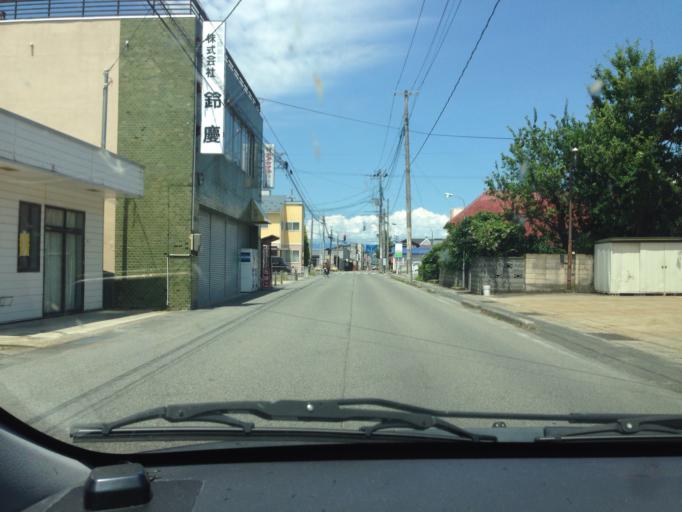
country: JP
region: Fukushima
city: Kitakata
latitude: 37.4893
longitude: 139.9181
